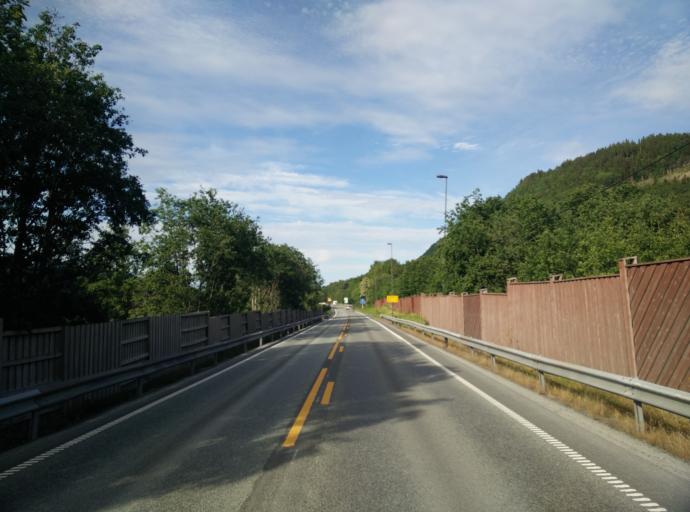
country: NO
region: Sor-Trondelag
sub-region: Orkdal
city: Orkanger
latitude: 63.3097
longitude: 9.8602
